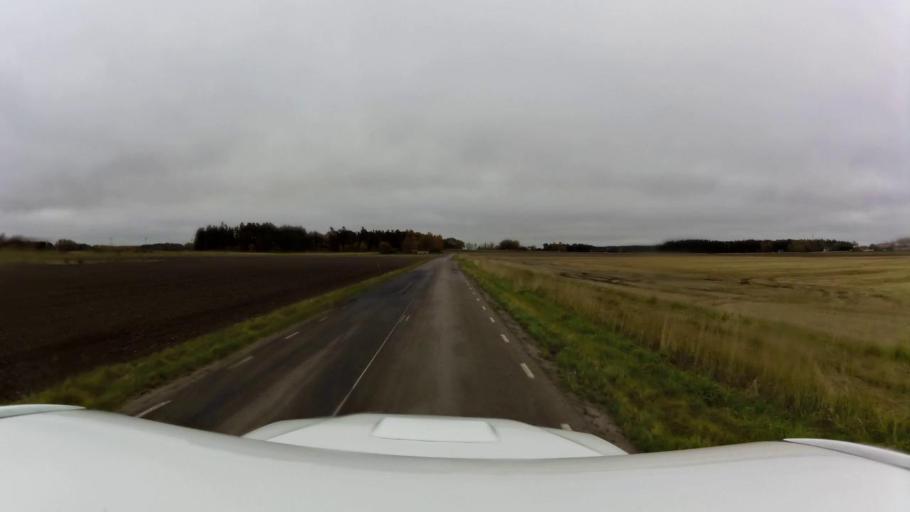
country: SE
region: OEstergoetland
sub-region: Linkopings Kommun
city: Linghem
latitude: 58.4357
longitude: 15.7164
